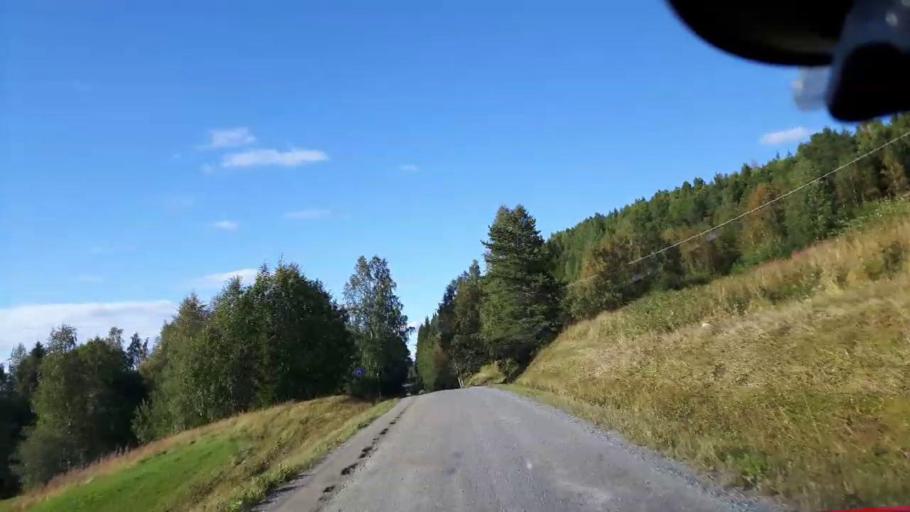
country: SE
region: Jaemtland
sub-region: Ragunda Kommun
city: Hammarstrand
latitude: 63.4967
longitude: 16.0372
